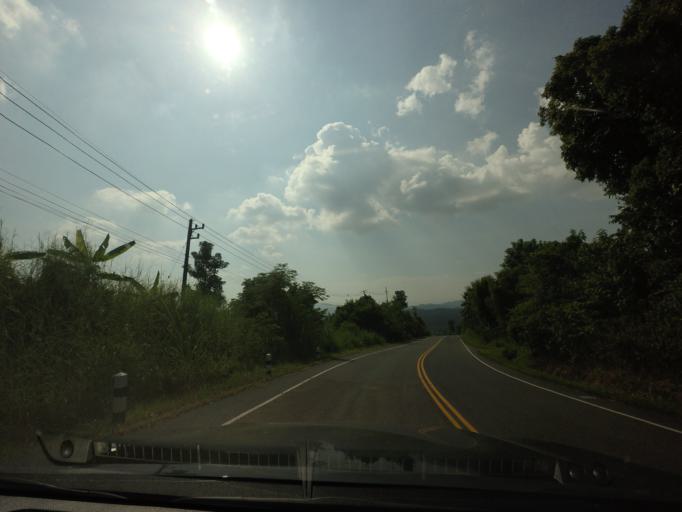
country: TH
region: Nan
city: Santi Suk
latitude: 18.9822
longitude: 100.9485
